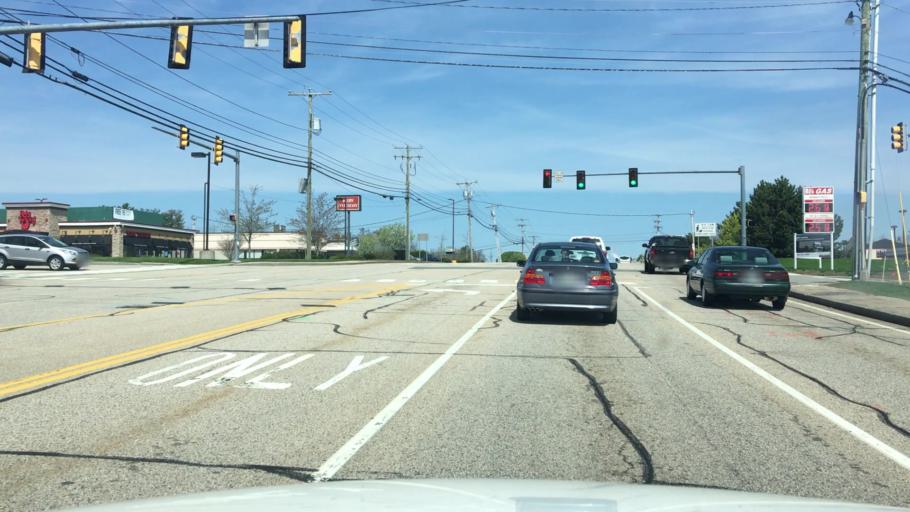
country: US
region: Maine
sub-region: York County
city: South Eliot
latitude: 43.0886
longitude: -70.7904
